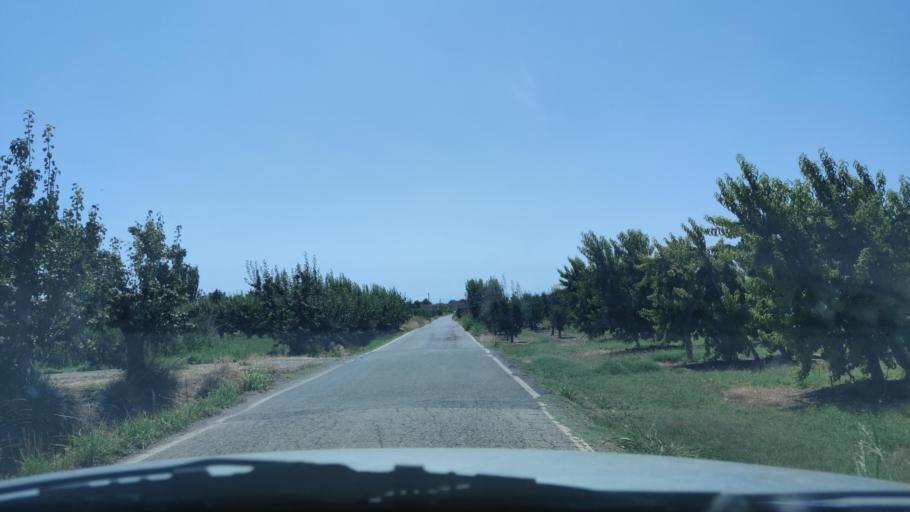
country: ES
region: Catalonia
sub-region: Provincia de Lleida
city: Torrefarrera
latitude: 41.6567
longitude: 0.5922
